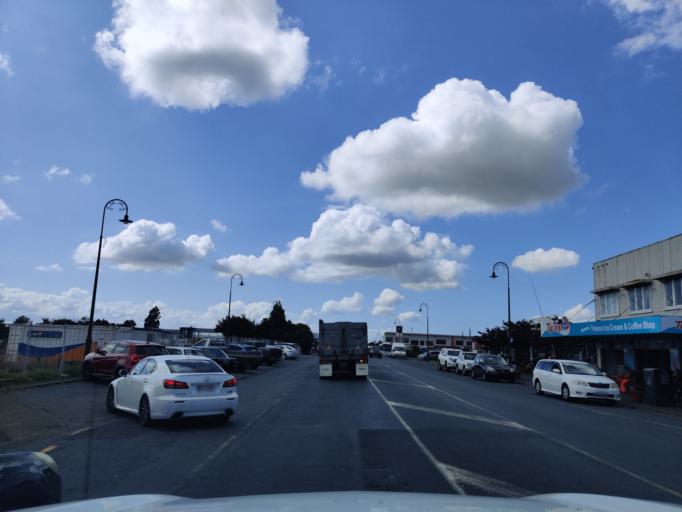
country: NZ
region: Auckland
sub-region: Auckland
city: Pukekohe East
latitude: -37.2457
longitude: 175.0219
